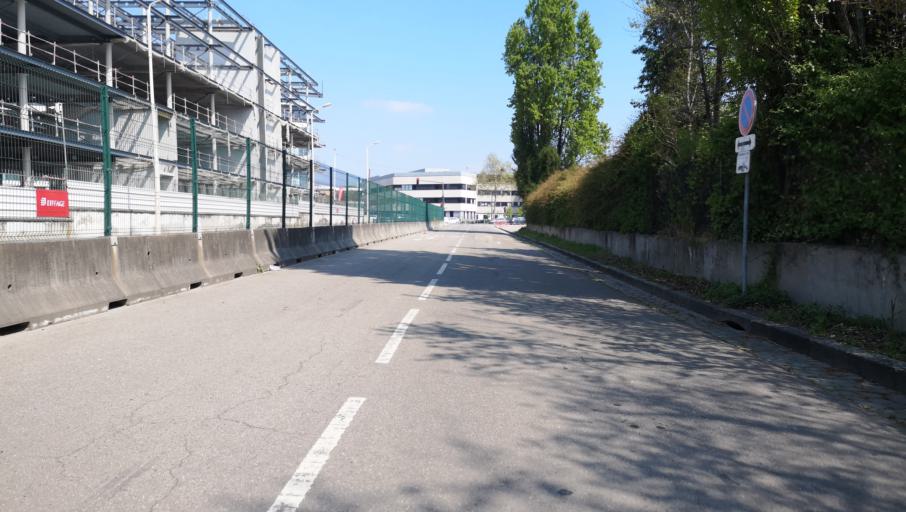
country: FR
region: Rhone-Alpes
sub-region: Departement du Rhone
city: Lyon
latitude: 45.7251
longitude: 4.8350
